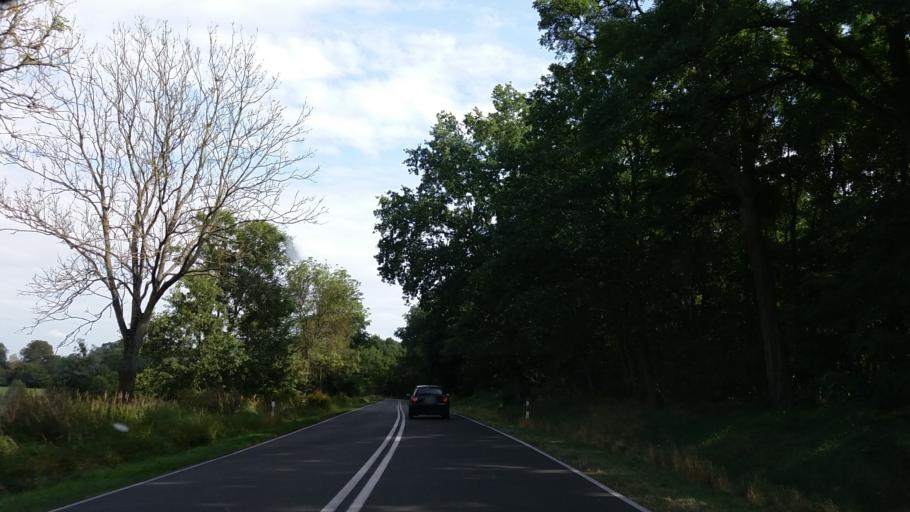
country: PL
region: West Pomeranian Voivodeship
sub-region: Powiat stargardzki
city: Suchan
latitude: 53.2102
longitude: 15.3189
